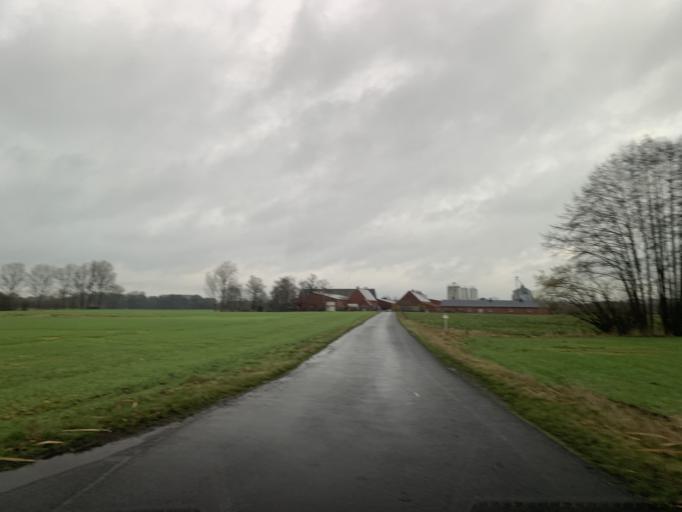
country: DE
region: North Rhine-Westphalia
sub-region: Regierungsbezirk Munster
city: Nordwalde
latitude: 52.1049
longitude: 7.4847
